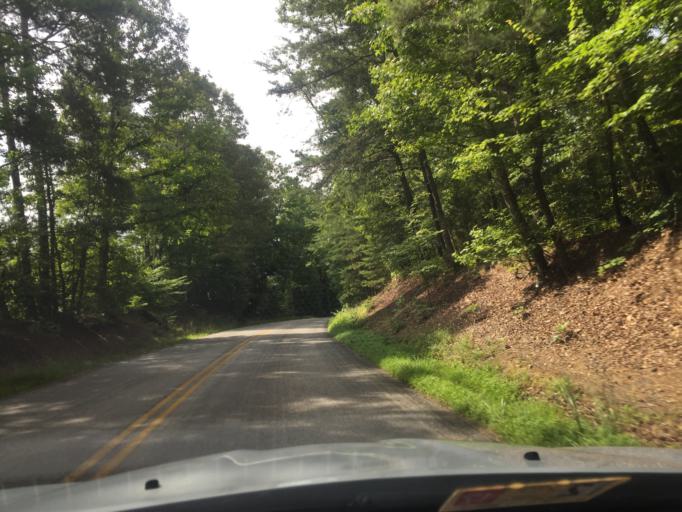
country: US
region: Virginia
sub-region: Charles City County
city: Charles City
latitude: 37.3962
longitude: -77.0167
